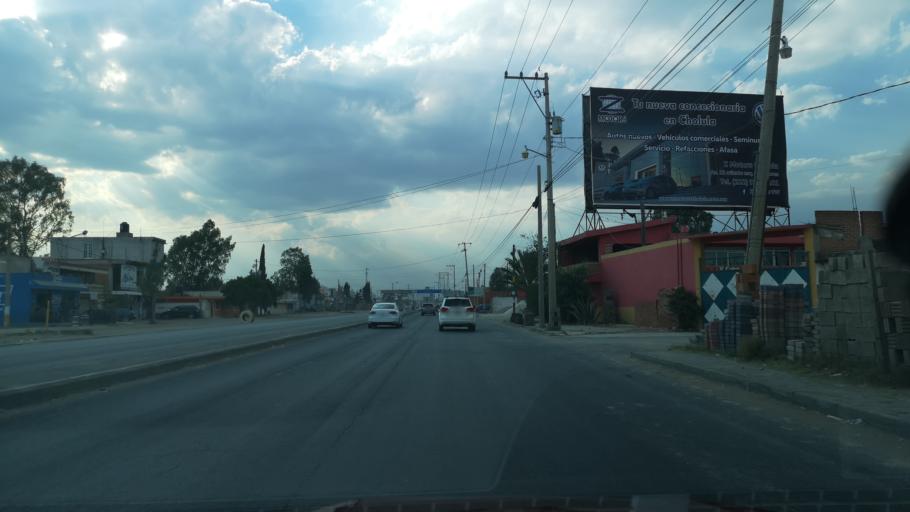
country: MX
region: Puebla
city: Cholula
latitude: 19.0755
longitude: -98.3206
